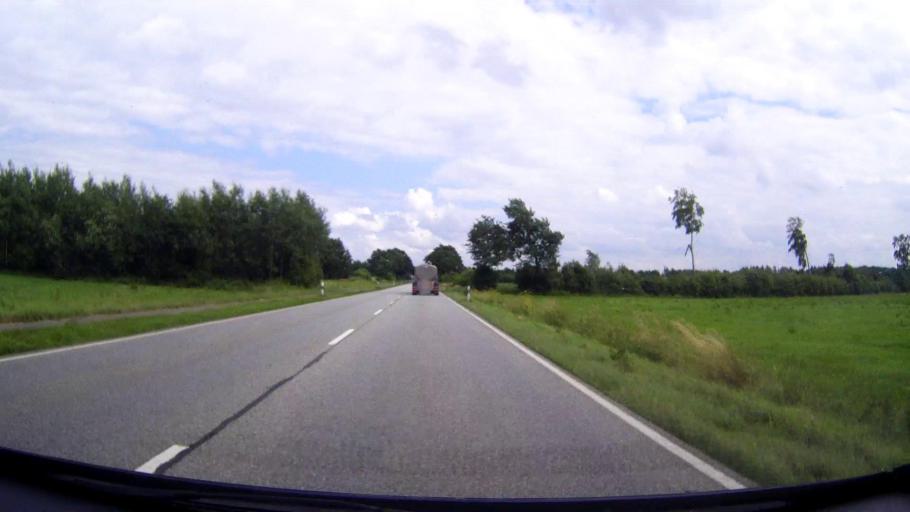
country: DE
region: Schleswig-Holstein
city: Wasbek
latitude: 54.0711
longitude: 9.8747
